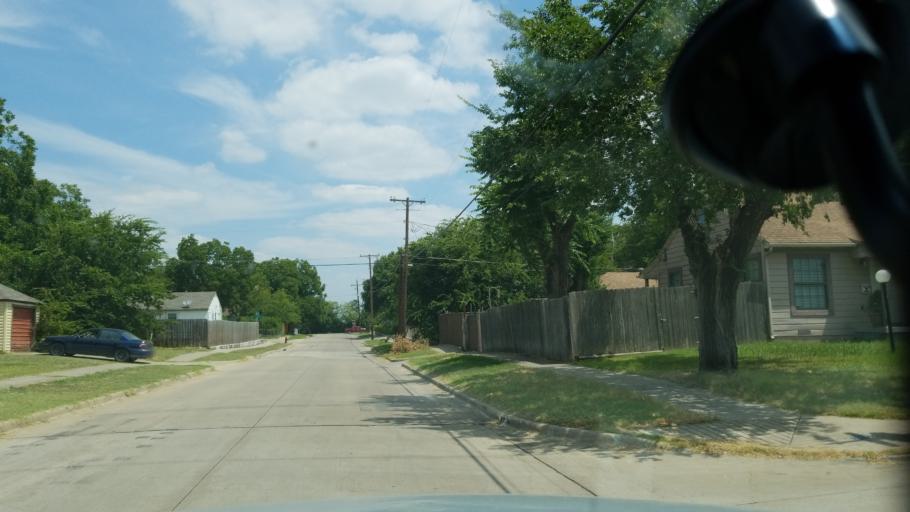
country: US
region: Texas
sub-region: Dallas County
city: Grand Prairie
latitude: 32.7546
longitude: -96.9842
